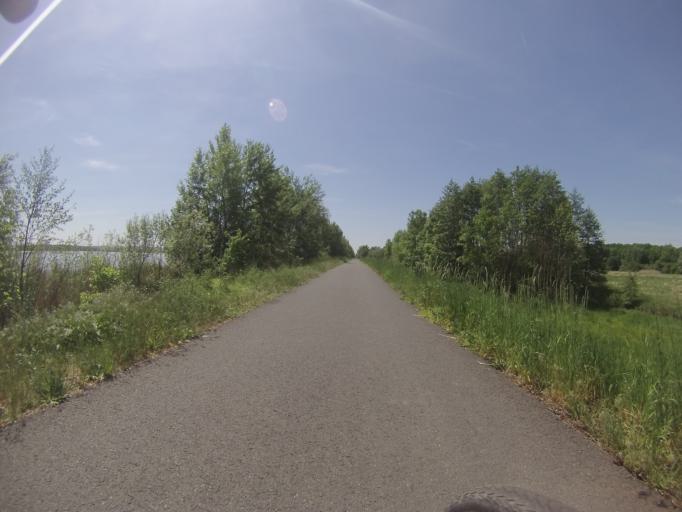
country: CZ
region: South Moravian
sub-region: Okres Breclav
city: Dolni Dunajovice
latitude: 48.9070
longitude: 16.5962
